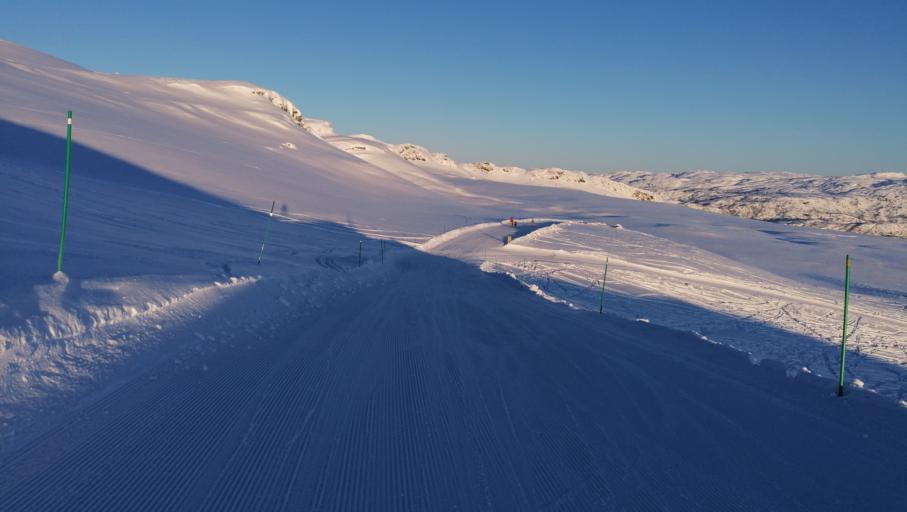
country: NO
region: Aust-Agder
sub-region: Bykle
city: Hovden
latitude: 59.5821
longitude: 7.3318
